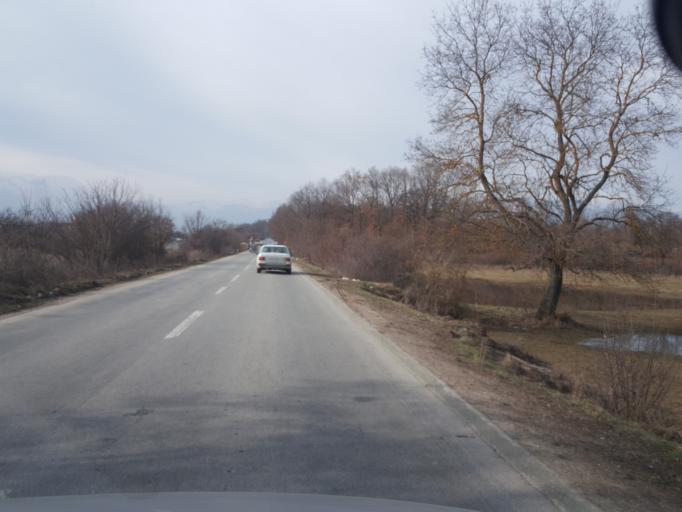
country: XK
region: Pec
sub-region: Komuna e Istogut
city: Istok
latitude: 42.6893
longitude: 20.5067
